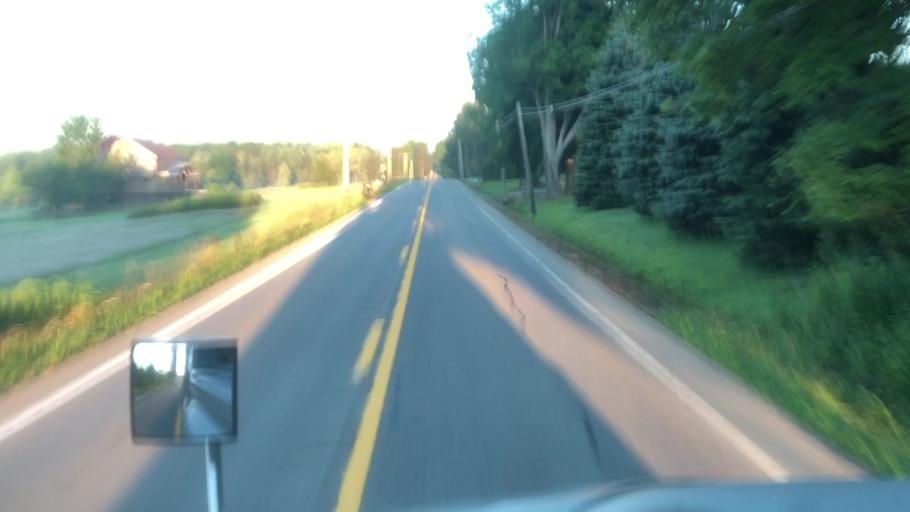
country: US
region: Pennsylvania
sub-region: Crawford County
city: Titusville
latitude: 41.5944
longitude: -79.6001
